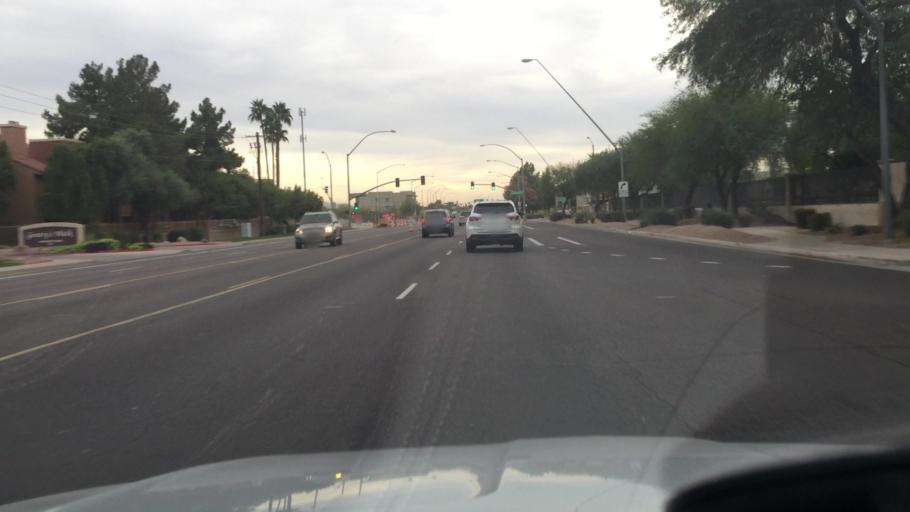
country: US
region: Arizona
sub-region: Maricopa County
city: Gilbert
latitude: 33.3913
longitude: -111.7539
